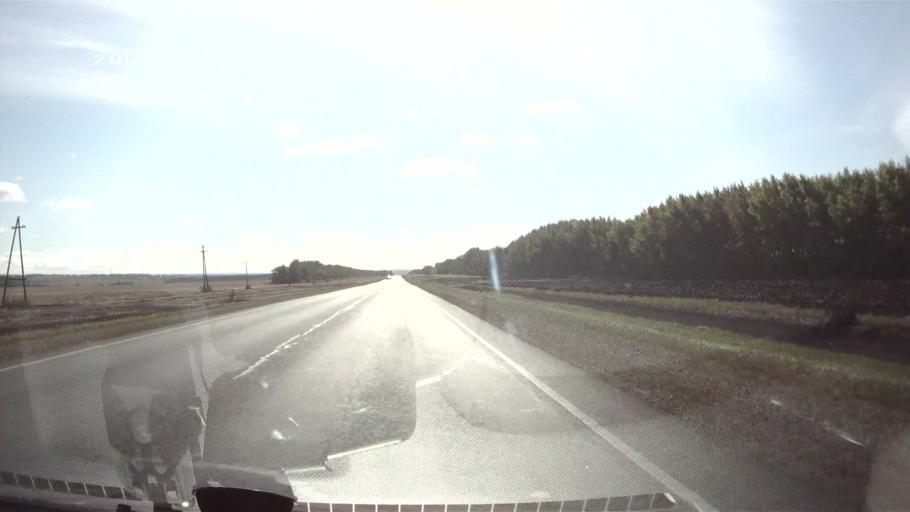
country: RU
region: Ulyanovsk
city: Tsil'na
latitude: 54.5682
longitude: 47.9131
